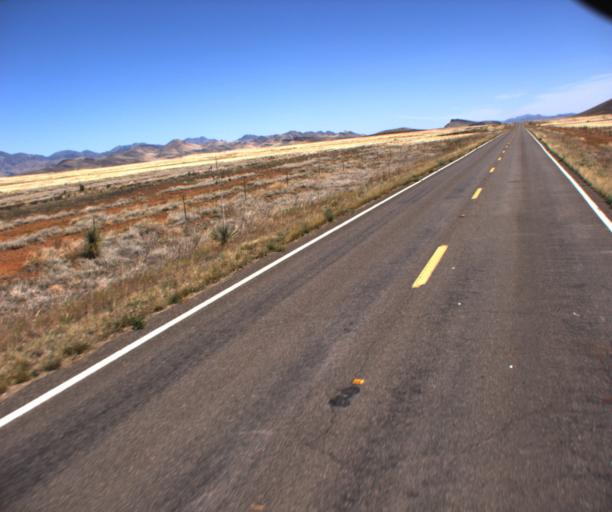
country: US
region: Arizona
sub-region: Cochise County
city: Douglas
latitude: 31.6038
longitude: -109.2285
